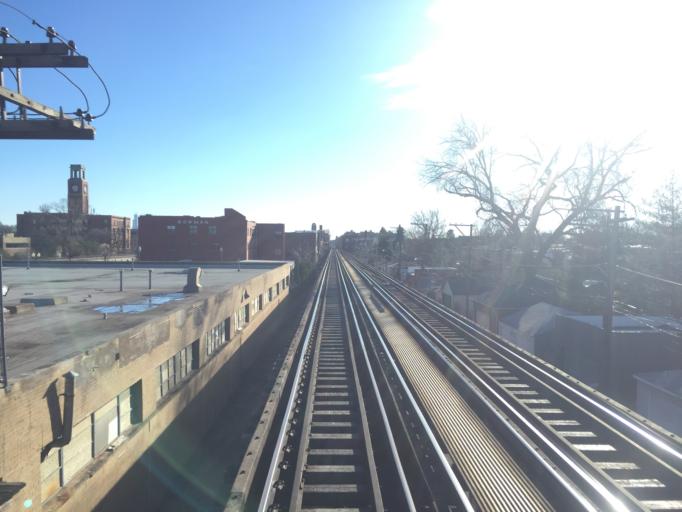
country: US
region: Illinois
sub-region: Cook County
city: Lincolnwood
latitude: 41.9607
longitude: -87.6751
